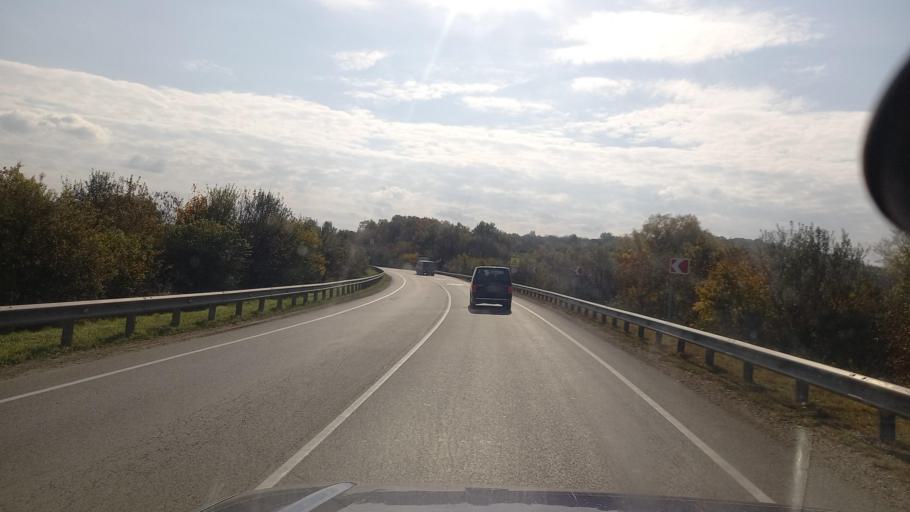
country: RU
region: Krasnodarskiy
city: Abinsk
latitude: 44.8517
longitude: 38.1348
